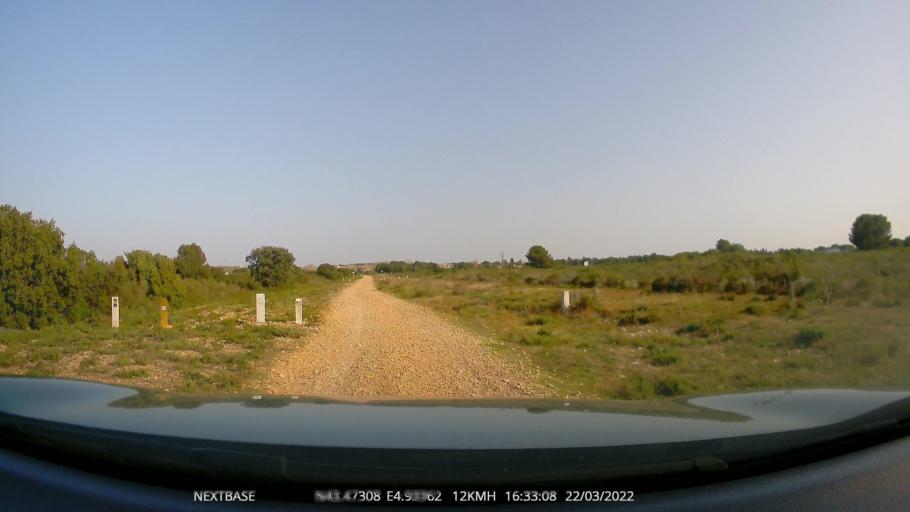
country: FR
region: Provence-Alpes-Cote d'Azur
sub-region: Departement des Bouches-du-Rhone
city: Fos-sur-Mer
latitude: 43.4731
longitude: 4.9336
